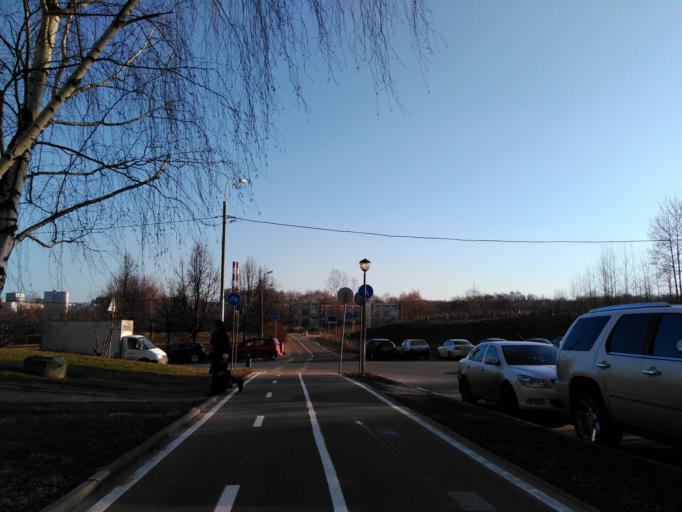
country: RU
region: Moscow
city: Zyuzino
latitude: 55.6336
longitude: 37.5882
